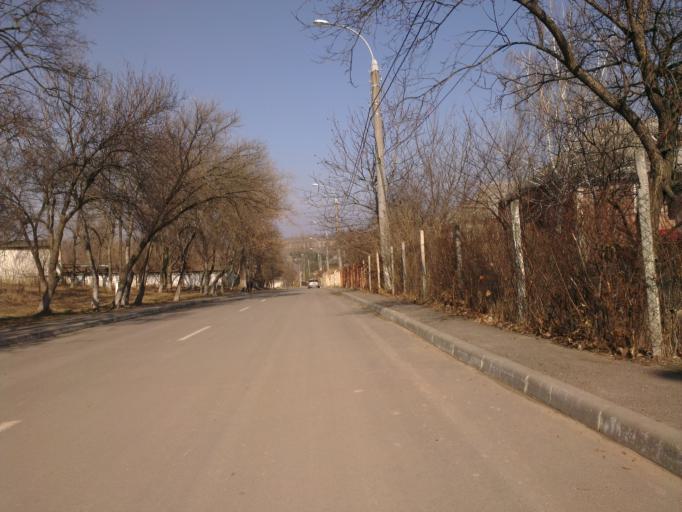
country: MD
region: Chisinau
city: Cricova
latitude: 47.1438
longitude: 28.8639
